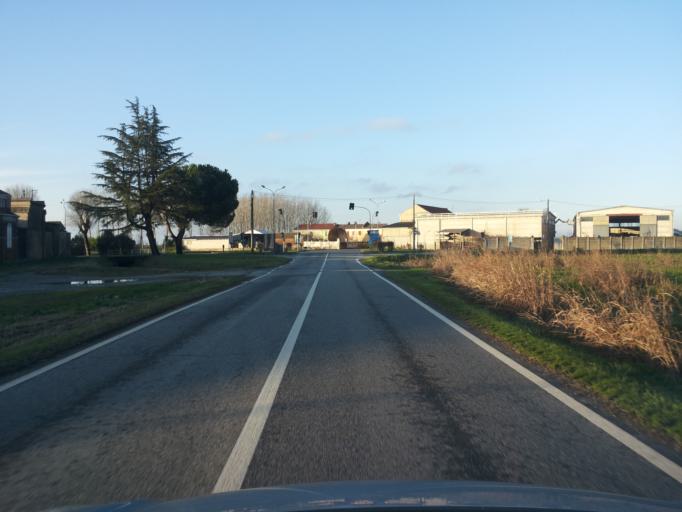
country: IT
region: Piedmont
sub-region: Provincia di Vercelli
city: Asigliano Vercellese
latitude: 45.2628
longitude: 8.4138
